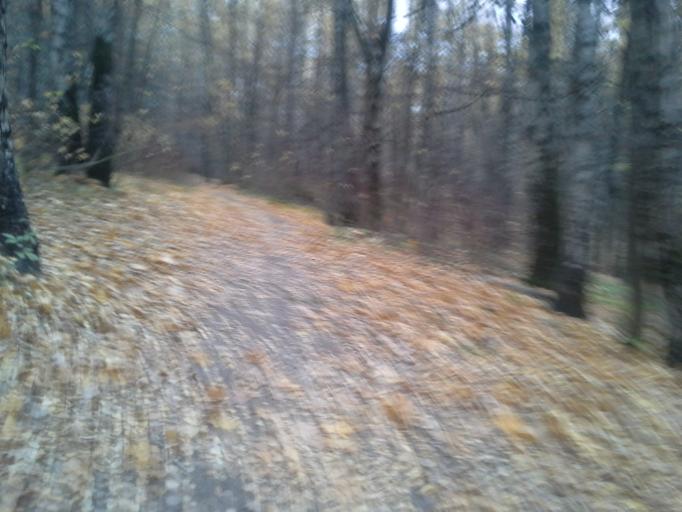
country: RU
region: Moscow
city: Zyuzino
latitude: 55.6446
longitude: 37.5749
